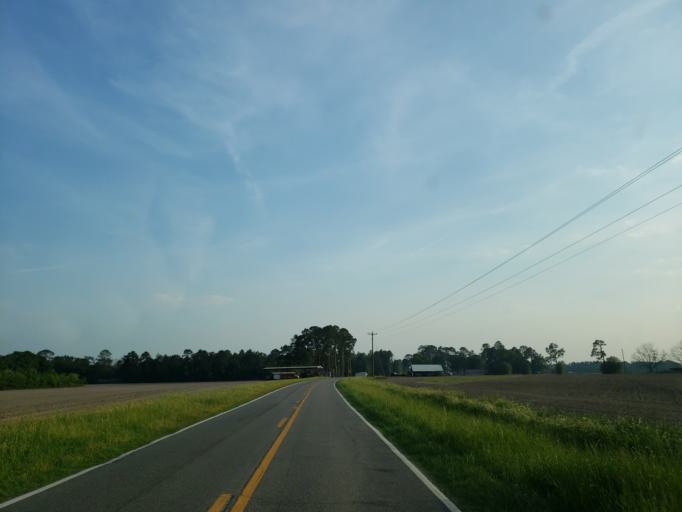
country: US
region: Georgia
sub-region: Cook County
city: Sparks
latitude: 31.2046
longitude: -83.4226
